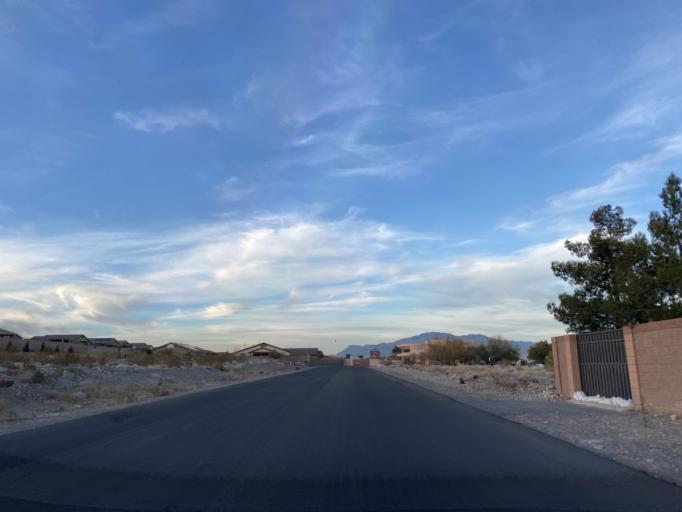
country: US
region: Nevada
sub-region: Clark County
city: Summerlin South
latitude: 36.2909
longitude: -115.3126
